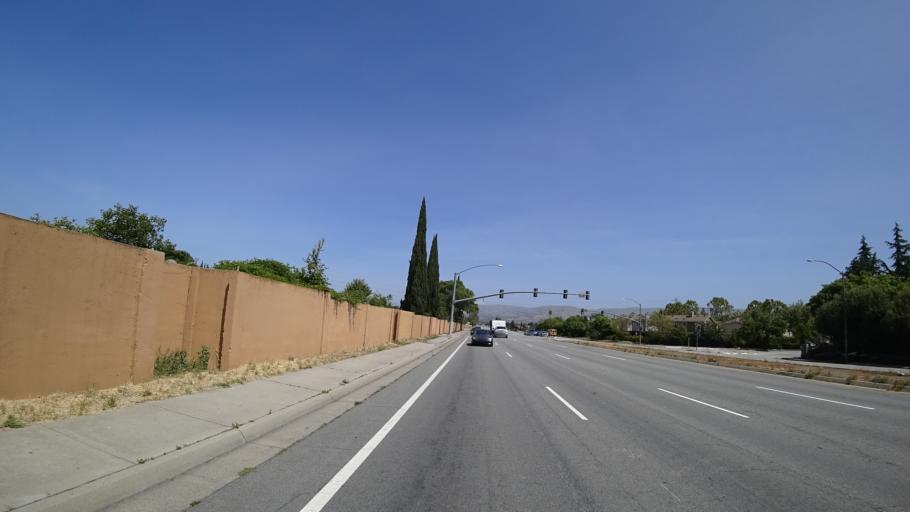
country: US
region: California
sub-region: Santa Clara County
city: Seven Trees
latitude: 37.3156
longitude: -121.8082
